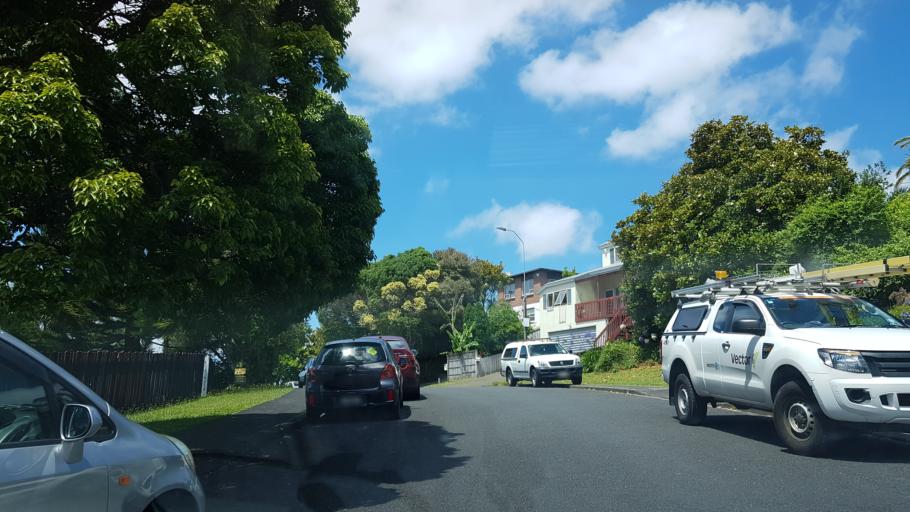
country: NZ
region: Auckland
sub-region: Auckland
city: North Shore
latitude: -36.7766
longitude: 174.7128
